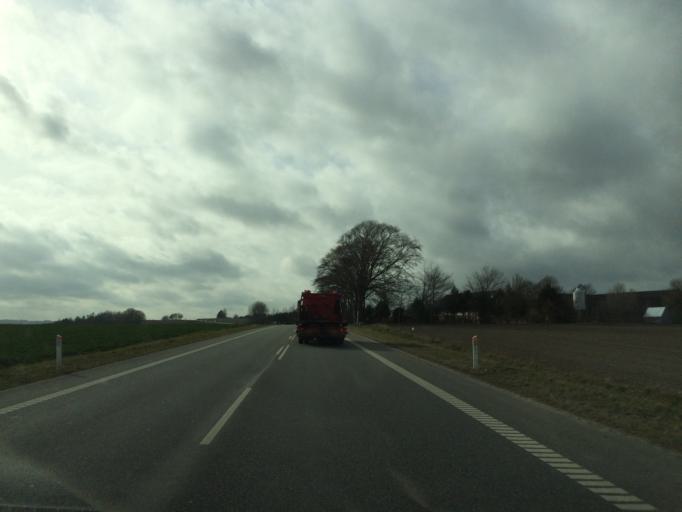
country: DK
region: Central Jutland
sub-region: Randers Kommune
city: Langa
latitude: 56.4792
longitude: 9.9008
